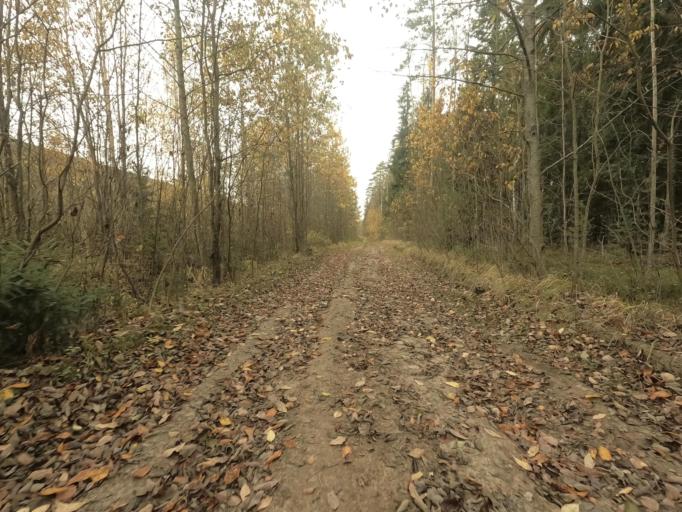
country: RU
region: Leningrad
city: Pavlovo
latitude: 59.7759
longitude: 30.9022
